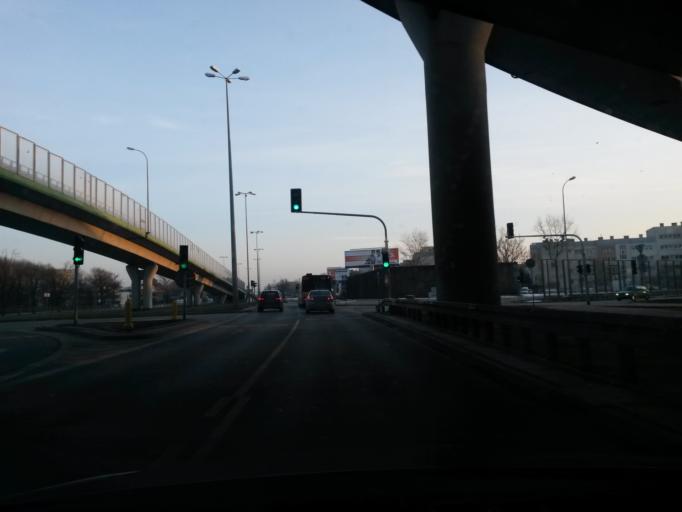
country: PL
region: Masovian Voivodeship
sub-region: Warszawa
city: Mokotow
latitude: 52.1973
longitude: 21.0514
